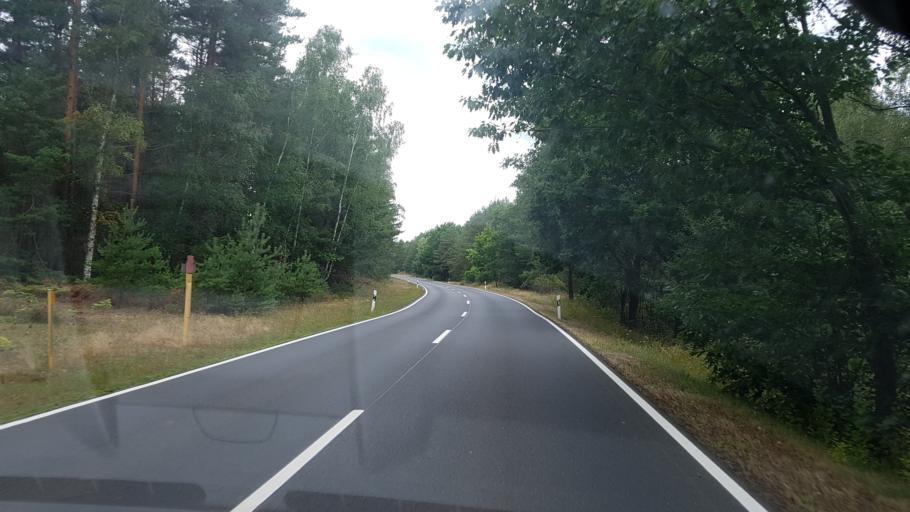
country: DE
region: Saxony
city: Boxberg
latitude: 51.3992
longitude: 14.5894
